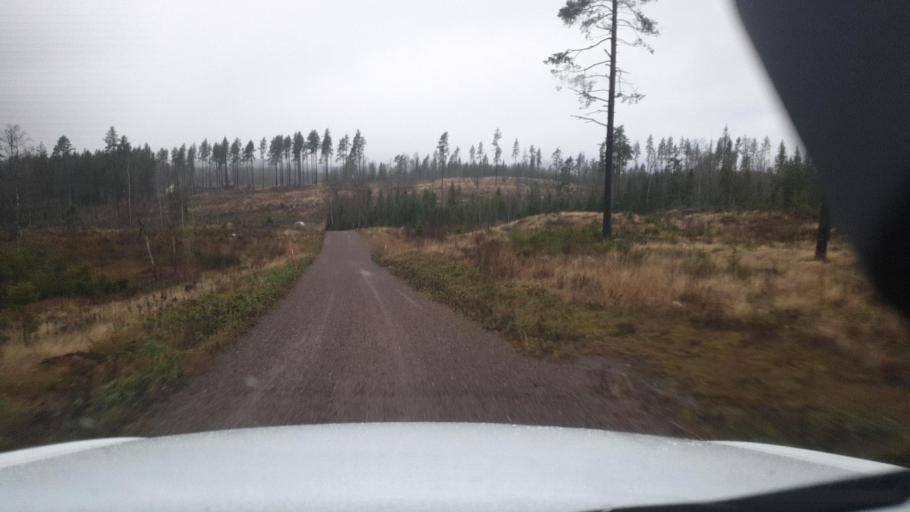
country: SE
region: Vaermland
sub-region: Torsby Kommun
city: Torsby
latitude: 59.9549
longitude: 12.7734
